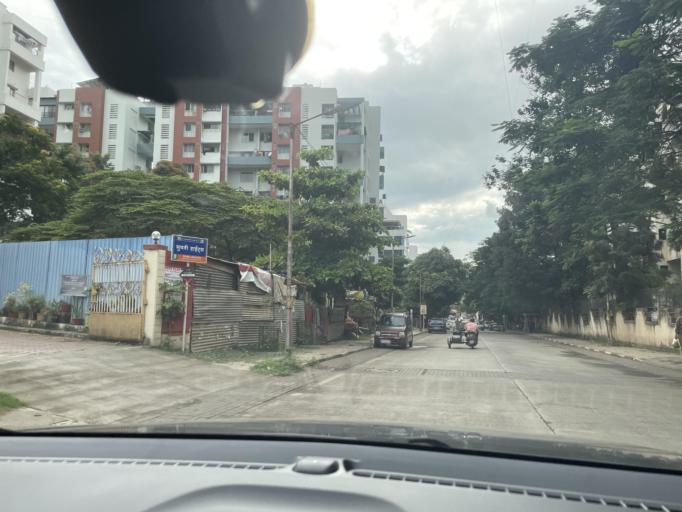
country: IN
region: Maharashtra
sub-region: Pune Division
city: Kharakvasla
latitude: 18.5112
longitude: 73.7798
